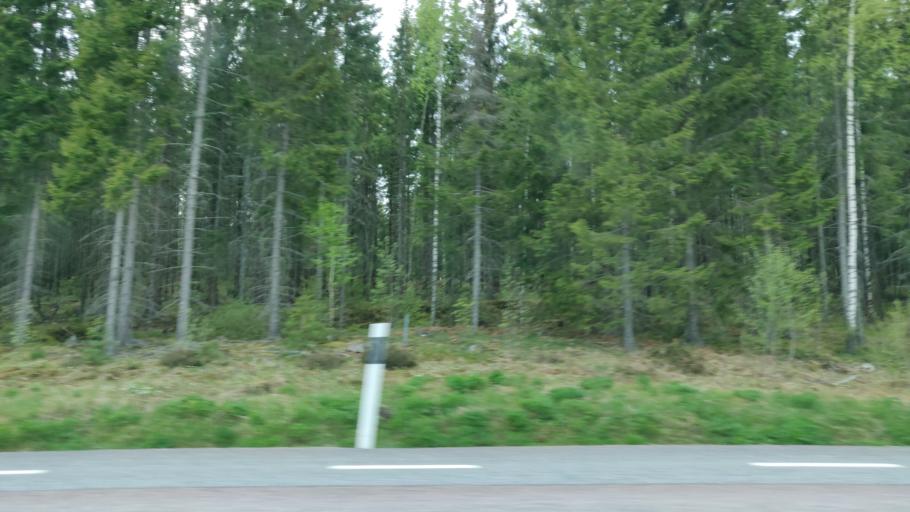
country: SE
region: Vaermland
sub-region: Forshaga Kommun
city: Deje
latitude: 59.6563
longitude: 13.4383
